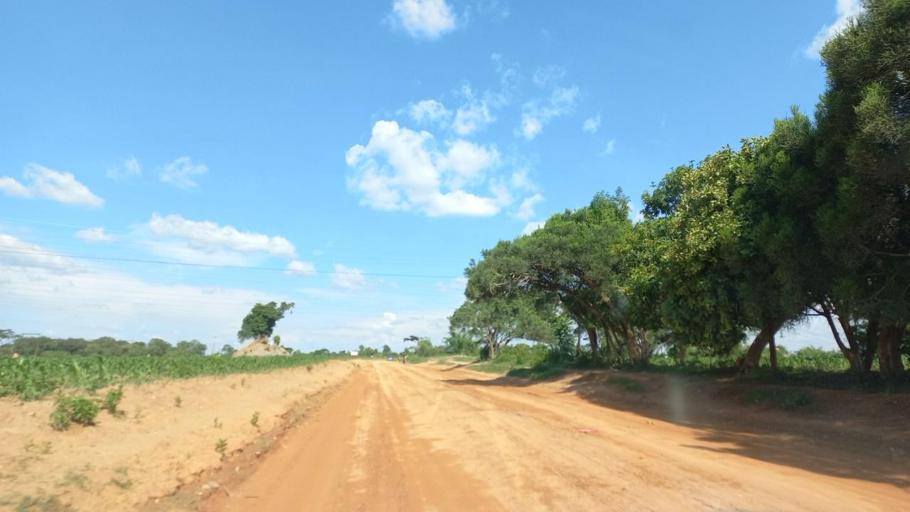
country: ZM
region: Copperbelt
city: Kitwe
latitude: -12.8711
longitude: 28.3429
